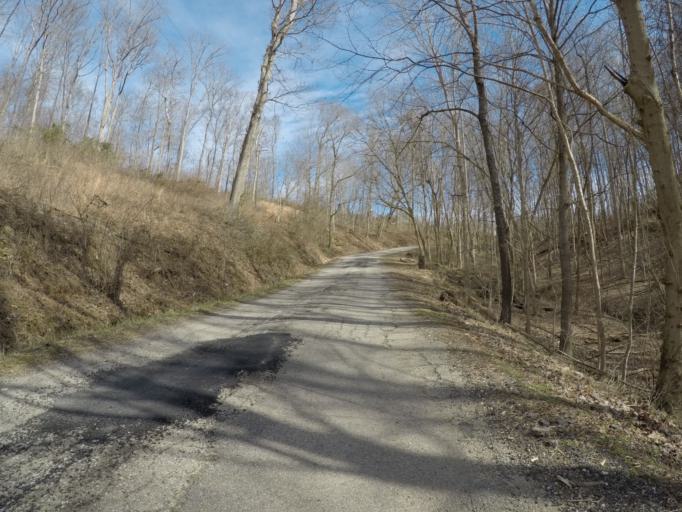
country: US
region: West Virginia
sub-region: Wayne County
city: Ceredo
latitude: 38.3481
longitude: -82.5499
